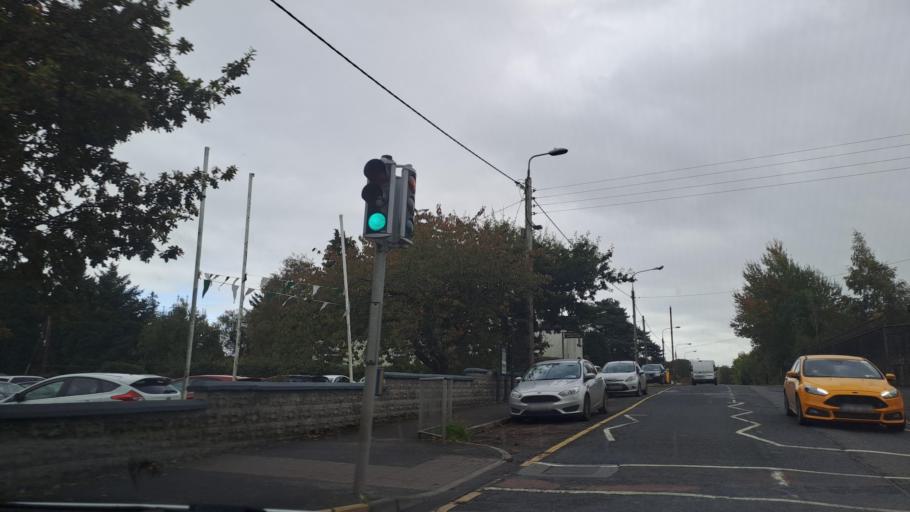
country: IE
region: Ulster
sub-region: An Cabhan
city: Cootehill
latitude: 54.0735
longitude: -7.0752
